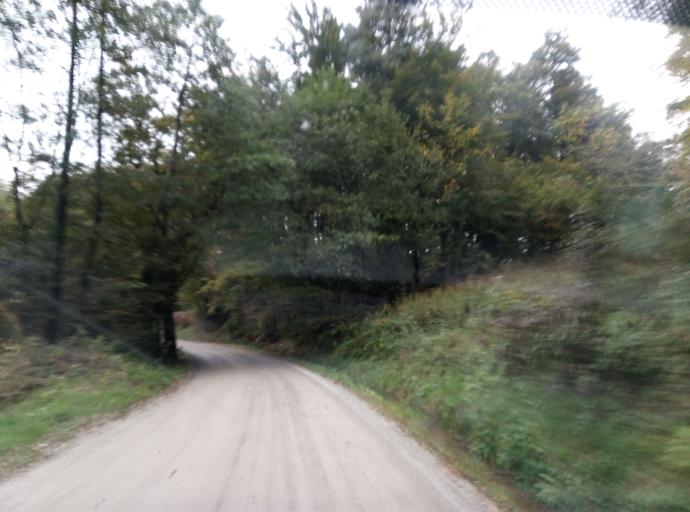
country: SI
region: Medvode
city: Zgornje Pirnice
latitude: 46.1361
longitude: 14.4825
